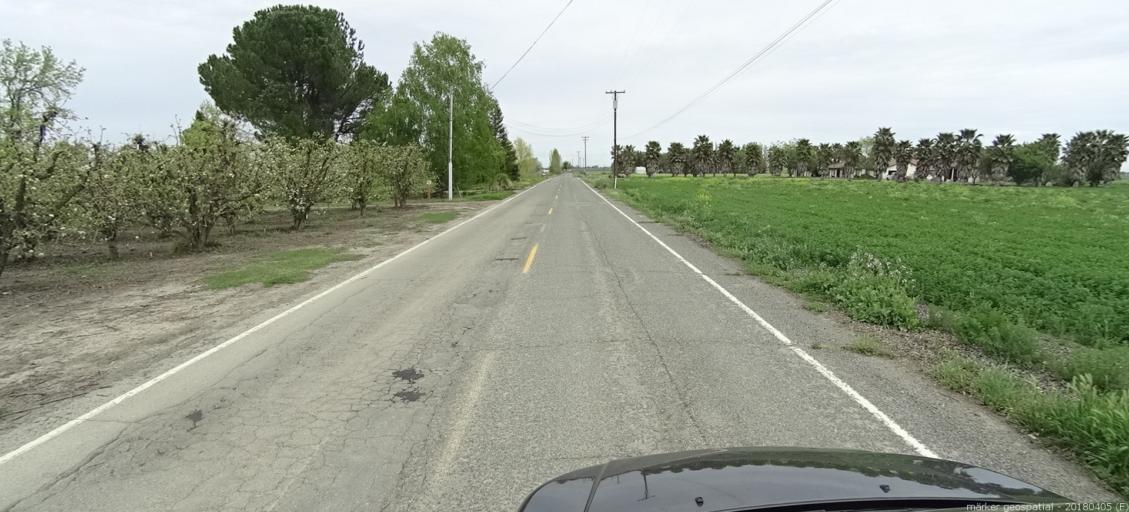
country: US
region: California
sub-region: Sacramento County
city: Walnut Grove
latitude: 38.2793
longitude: -121.5387
